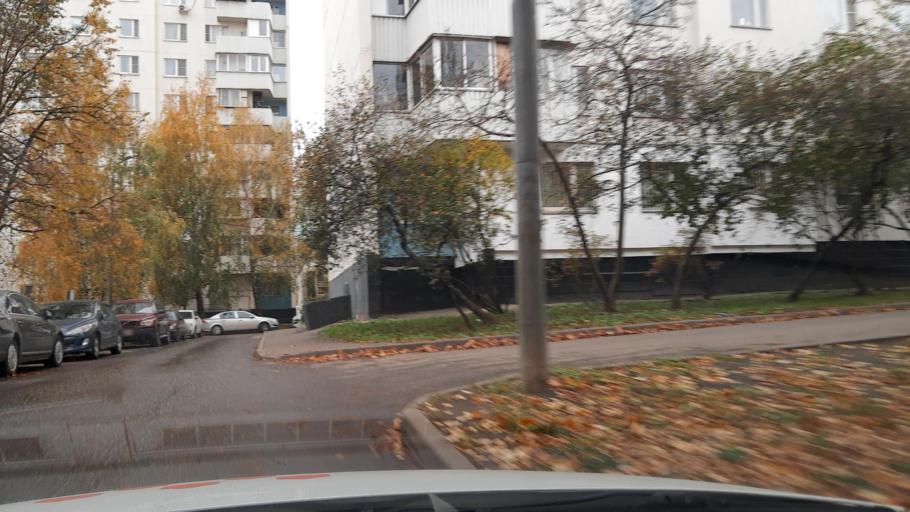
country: RU
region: Moscow
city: Orekhovo-Borisovo
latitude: 55.5973
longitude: 37.7215
